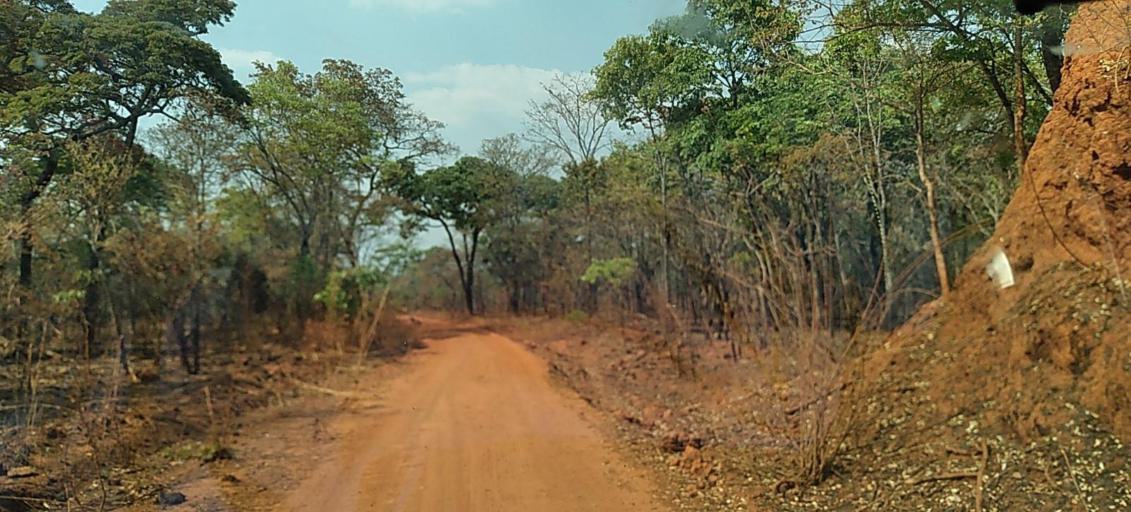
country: ZM
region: North-Western
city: Kasempa
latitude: -13.3154
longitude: 26.0579
